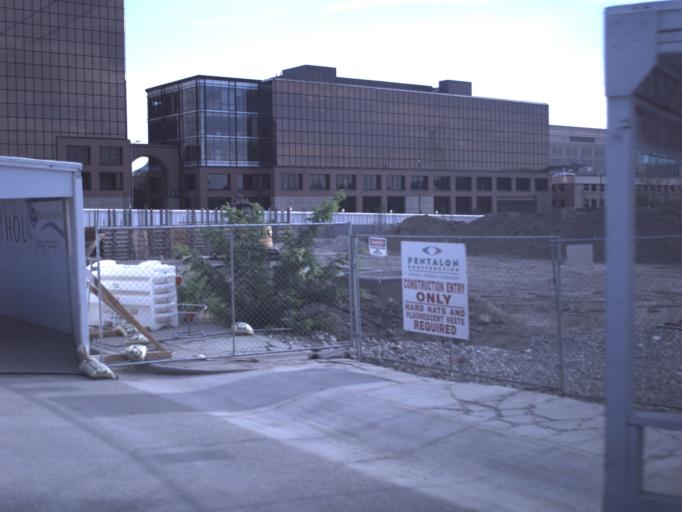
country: US
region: Utah
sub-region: Salt Lake County
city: Salt Lake City
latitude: 40.7724
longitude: -111.8998
